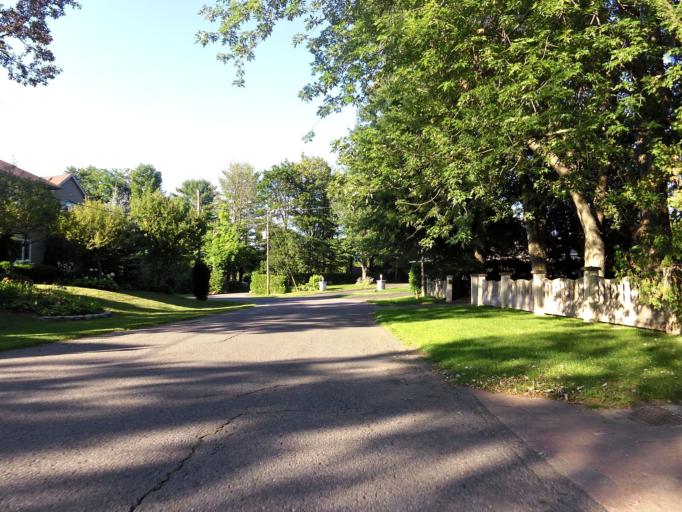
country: CA
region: Ontario
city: Ottawa
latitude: 45.3429
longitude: -75.6985
